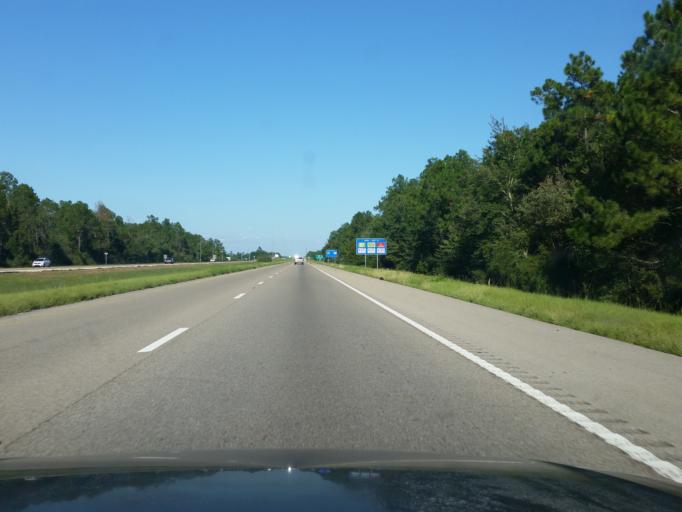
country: US
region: Mississippi
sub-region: Hancock County
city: Kiln
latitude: 30.3551
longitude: -89.4330
